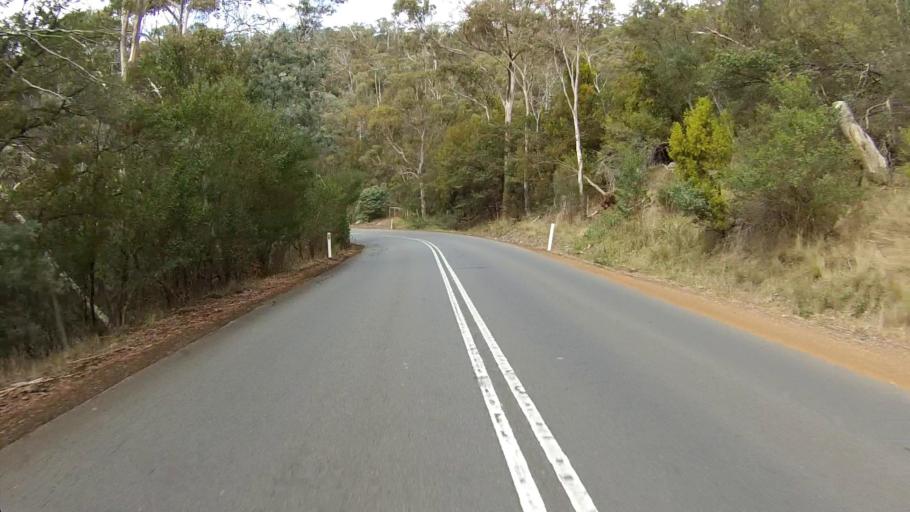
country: AU
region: Tasmania
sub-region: Clarence
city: Lindisfarne
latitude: -42.7806
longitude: 147.3698
